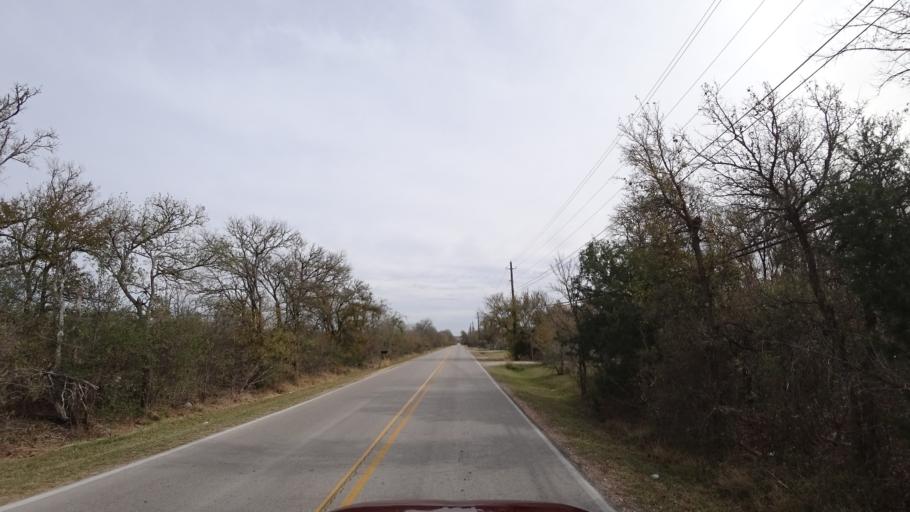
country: US
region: Texas
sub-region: Travis County
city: Garfield
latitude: 30.1365
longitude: -97.6173
